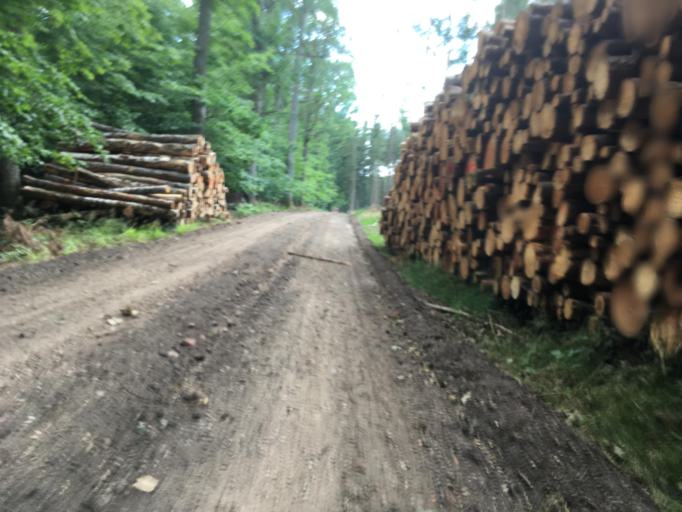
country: DE
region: Brandenburg
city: Joachimsthal
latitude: 52.9208
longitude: 13.7469
